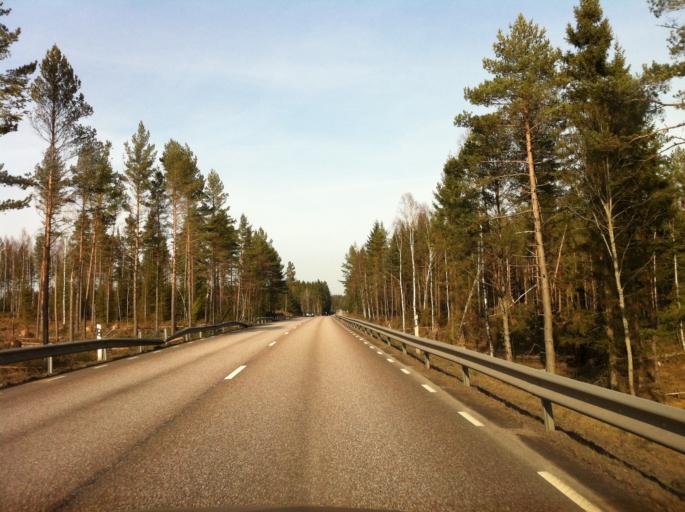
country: SE
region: Vaestra Goetaland
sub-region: Skovde Kommun
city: Skultorp
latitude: 58.2681
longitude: 13.8099
